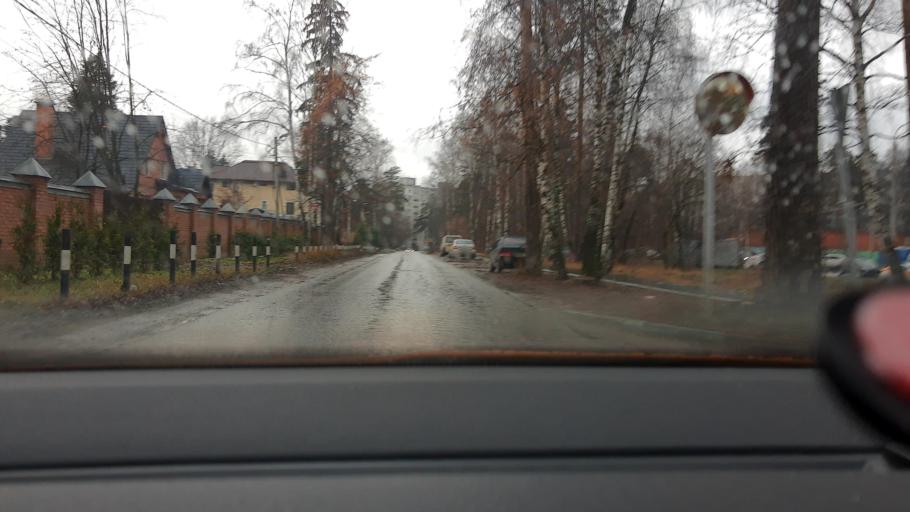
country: RU
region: Moskovskaya
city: Yubileyny
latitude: 55.9294
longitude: 37.8402
